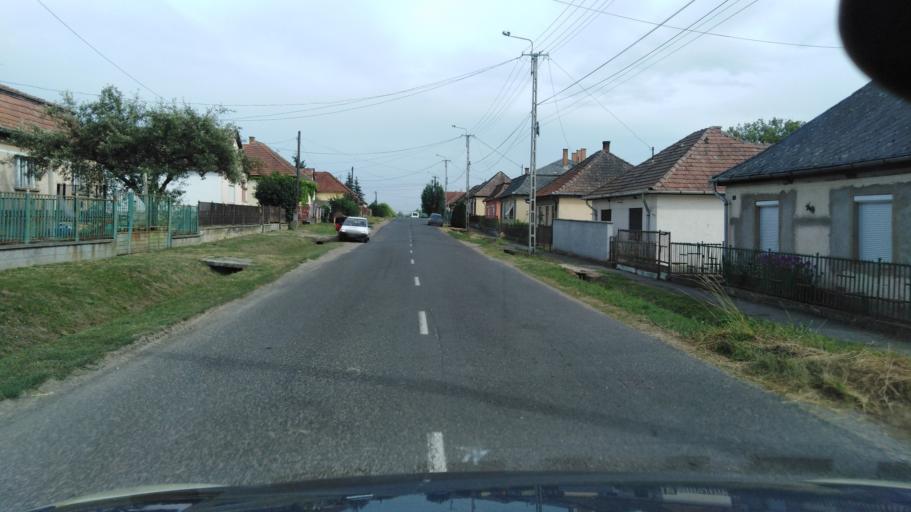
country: HU
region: Nograd
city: Karancskeszi
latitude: 48.2085
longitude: 19.6041
